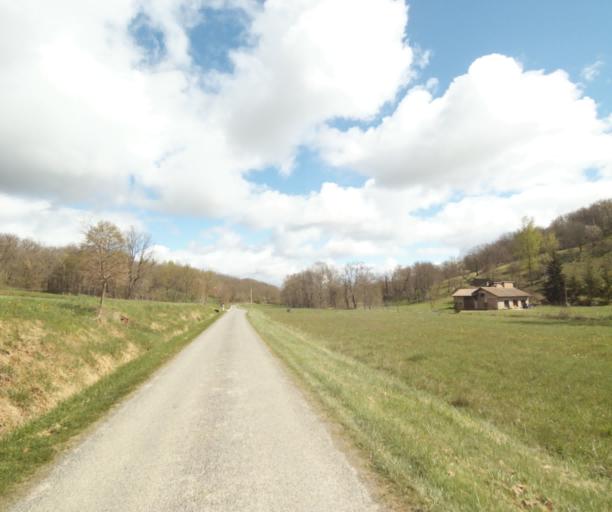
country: FR
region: Midi-Pyrenees
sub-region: Departement de l'Ariege
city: Saverdun
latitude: 43.1794
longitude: 1.5520
